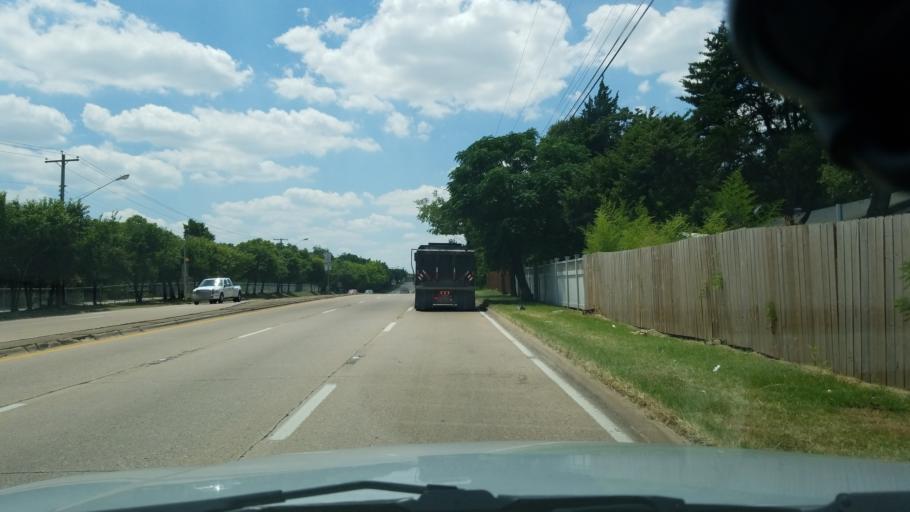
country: US
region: Texas
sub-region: Dallas County
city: Cockrell Hill
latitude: 32.6914
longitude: -96.8746
